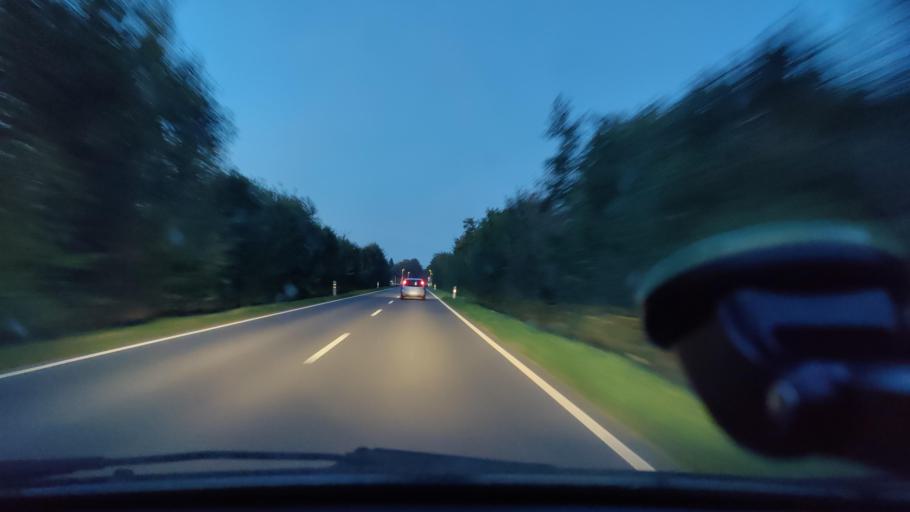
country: DE
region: North Rhine-Westphalia
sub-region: Regierungsbezirk Munster
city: Sudlohn
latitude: 51.9043
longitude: 6.8649
